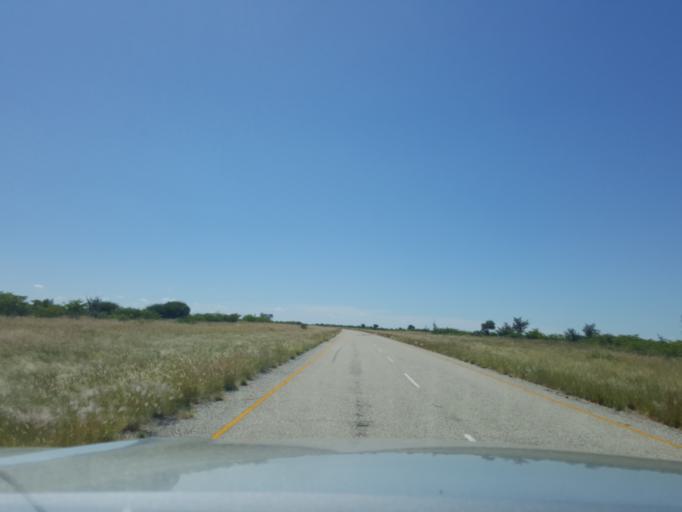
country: BW
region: Central
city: Gweta
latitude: -20.2308
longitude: 24.9715
